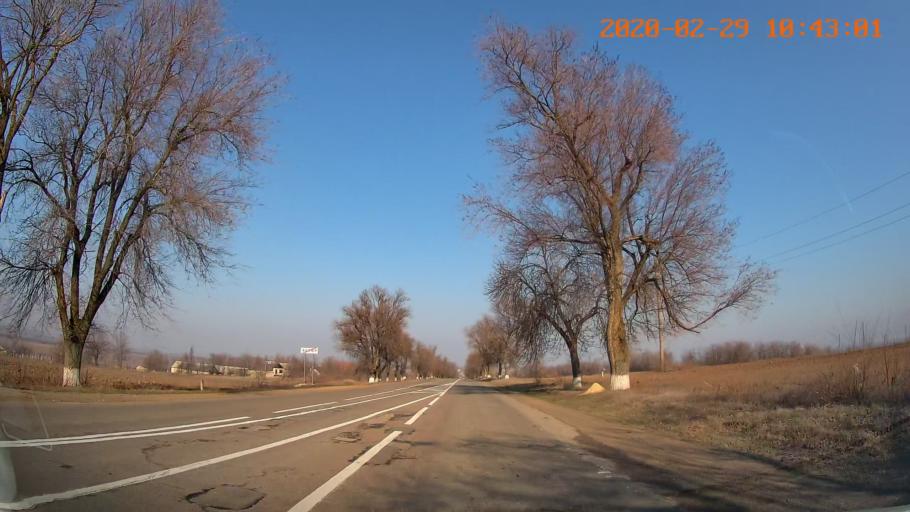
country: MD
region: Telenesti
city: Grigoriopol
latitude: 47.0566
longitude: 29.4055
